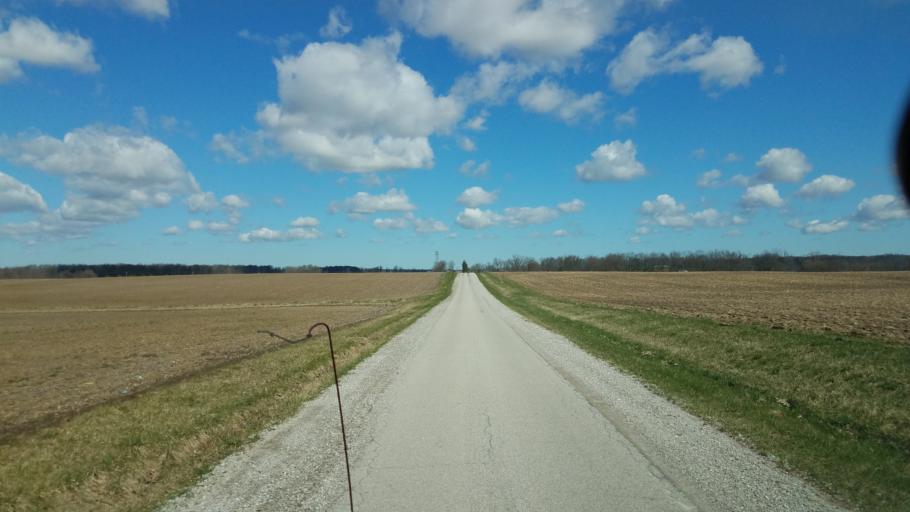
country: US
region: Ohio
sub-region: Sandusky County
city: Mount Carmel
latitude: 41.1183
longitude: -82.9384
